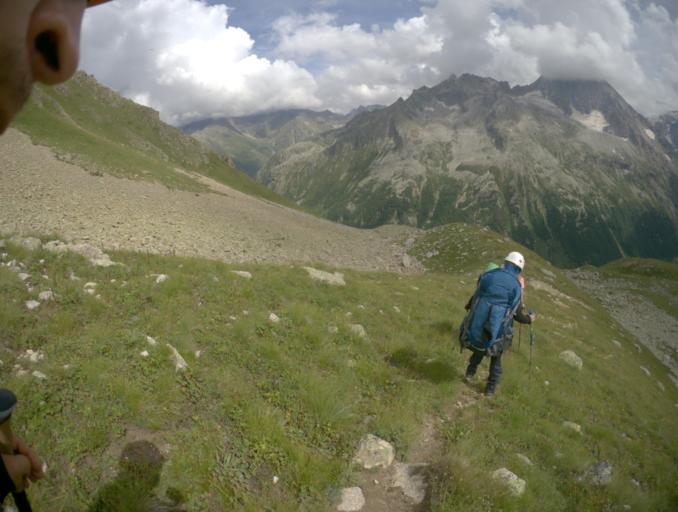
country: RU
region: Karachayevo-Cherkesiya
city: Uchkulan
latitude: 43.2696
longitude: 42.1272
